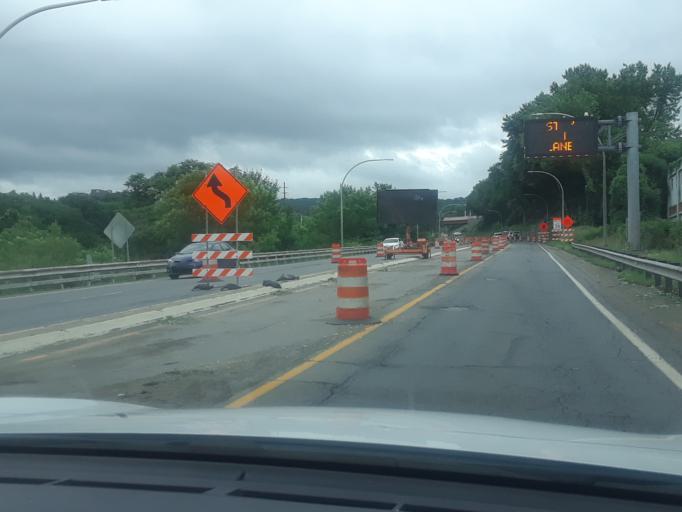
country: US
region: Pennsylvania
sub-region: Lackawanna County
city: Scranton
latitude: 41.4021
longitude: -75.6560
